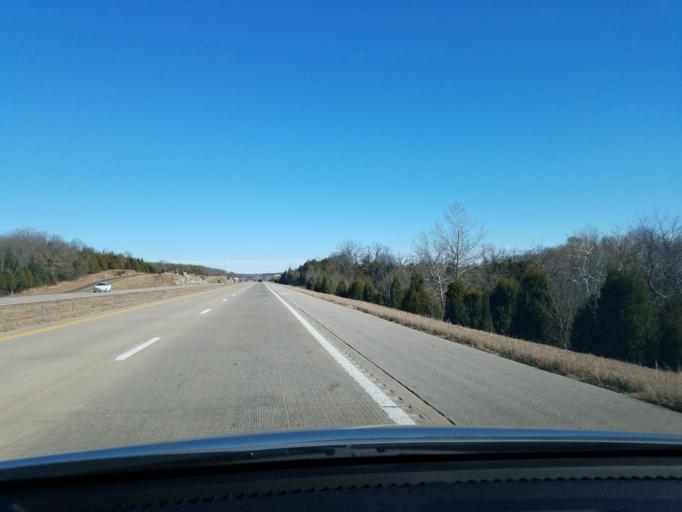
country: US
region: Missouri
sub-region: Laclede County
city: Lebanon
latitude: 37.7571
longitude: -92.5450
